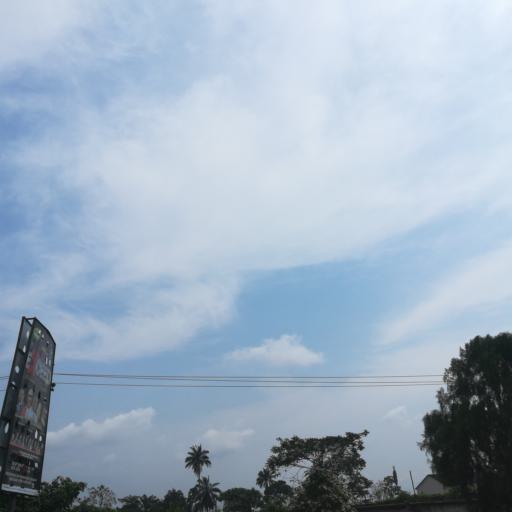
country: NG
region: Rivers
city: Port Harcourt
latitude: 4.8545
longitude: 7.0222
